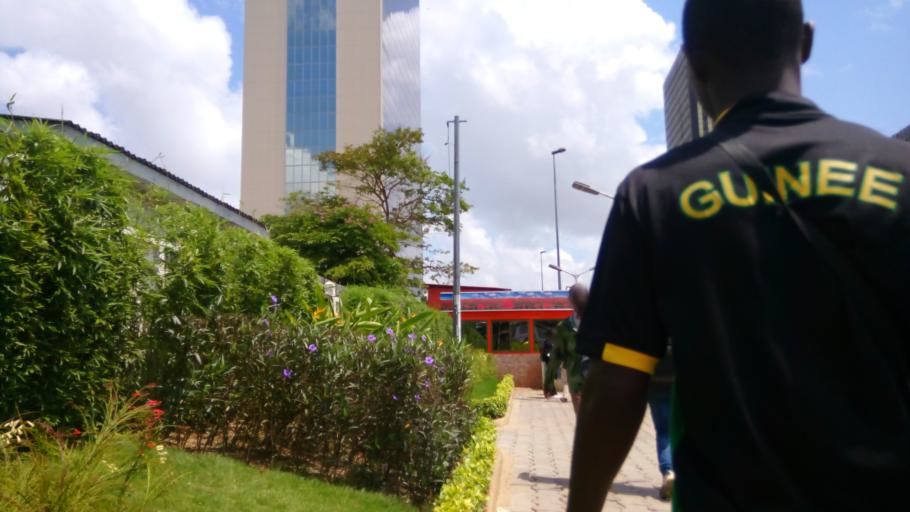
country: CI
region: Lagunes
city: Abidjan
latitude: 5.3316
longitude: -4.0209
